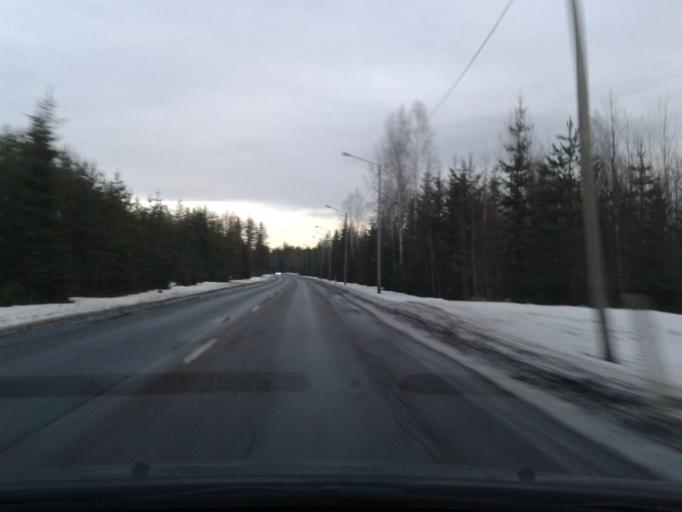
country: SE
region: Vaesternorrland
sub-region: Solleftea Kommun
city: Solleftea
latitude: 63.1512
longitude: 17.3361
